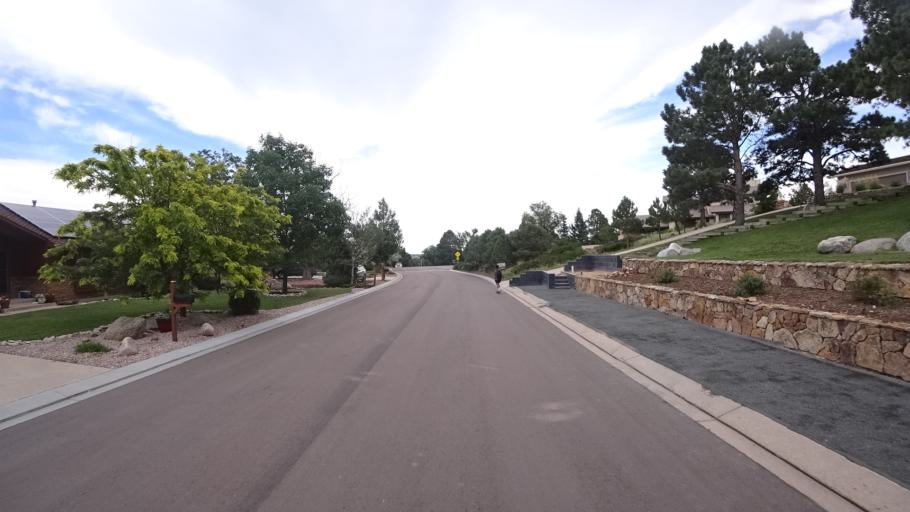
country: US
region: Colorado
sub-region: El Paso County
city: Colorado Springs
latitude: 38.9052
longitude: -104.8420
